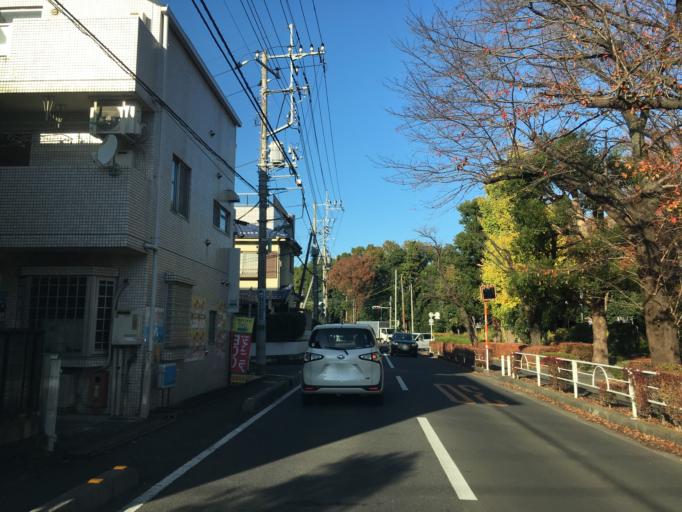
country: JP
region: Saitama
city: Tokorozawa
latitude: 35.8024
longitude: 139.4633
